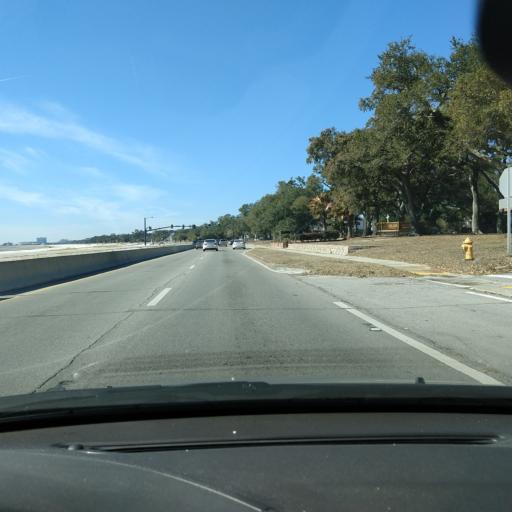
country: US
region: Mississippi
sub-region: Harrison County
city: Gulfport
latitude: 30.3751
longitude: -89.0586
